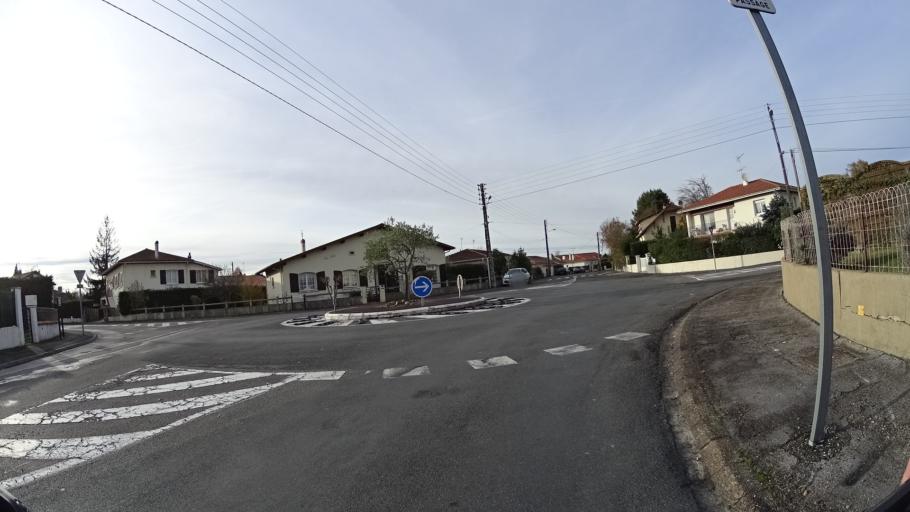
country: FR
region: Aquitaine
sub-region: Departement des Landes
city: Saint-Paul-les-Dax
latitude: 43.7296
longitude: -1.0549
